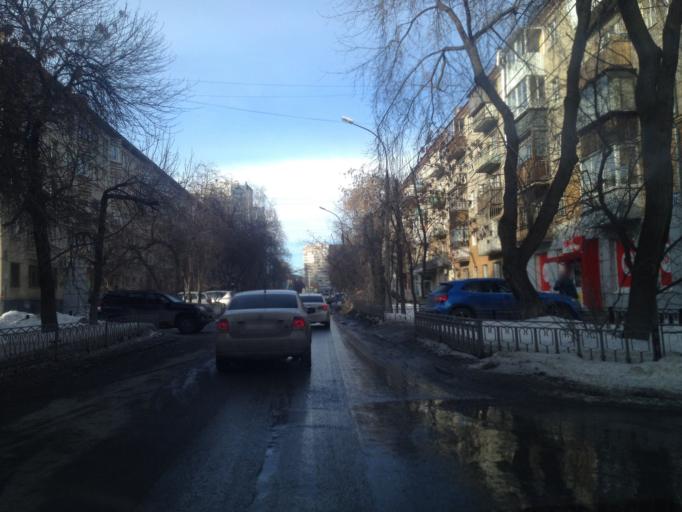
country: RU
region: Sverdlovsk
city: Yekaterinburg
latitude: 56.8440
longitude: 60.6247
